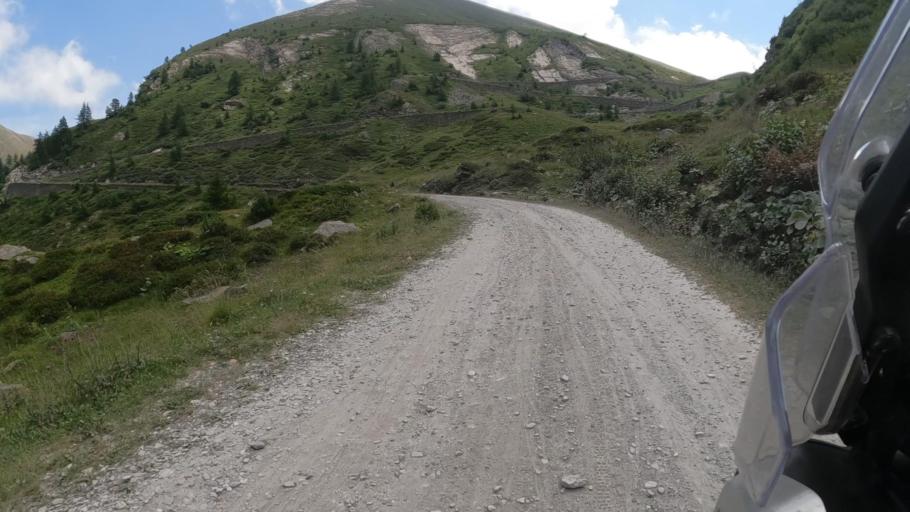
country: IT
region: Piedmont
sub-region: Provincia di Torino
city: Usseaux
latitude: 45.0740
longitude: 7.0528
